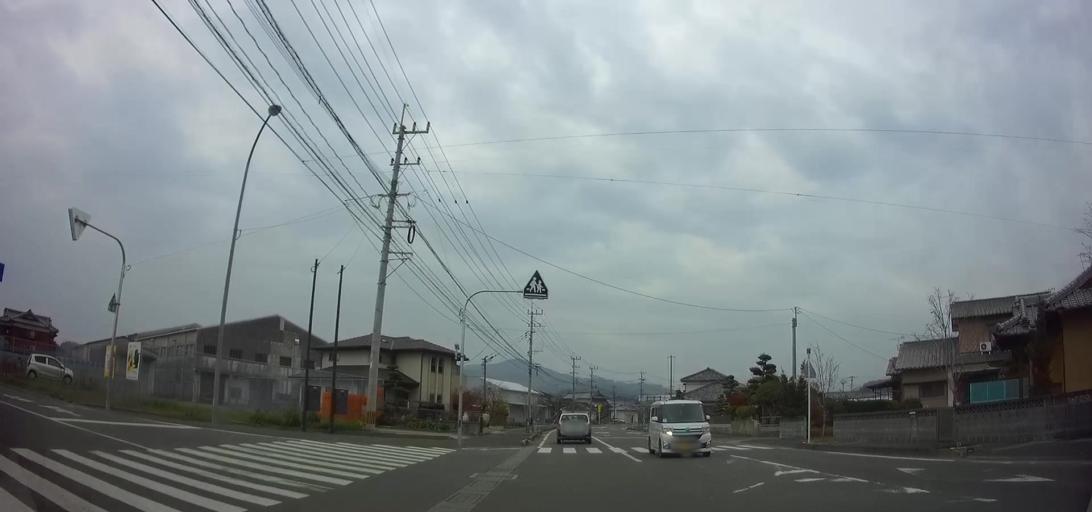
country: JP
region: Nagasaki
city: Shimabara
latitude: 32.6555
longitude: 130.2533
